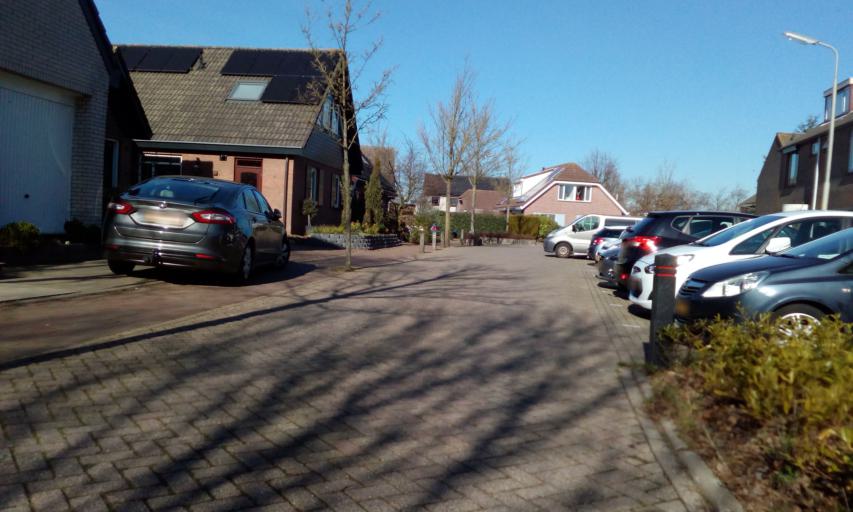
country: NL
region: South Holland
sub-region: Gemeente Lansingerland
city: Bleiswijk
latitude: 52.0059
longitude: 4.5790
